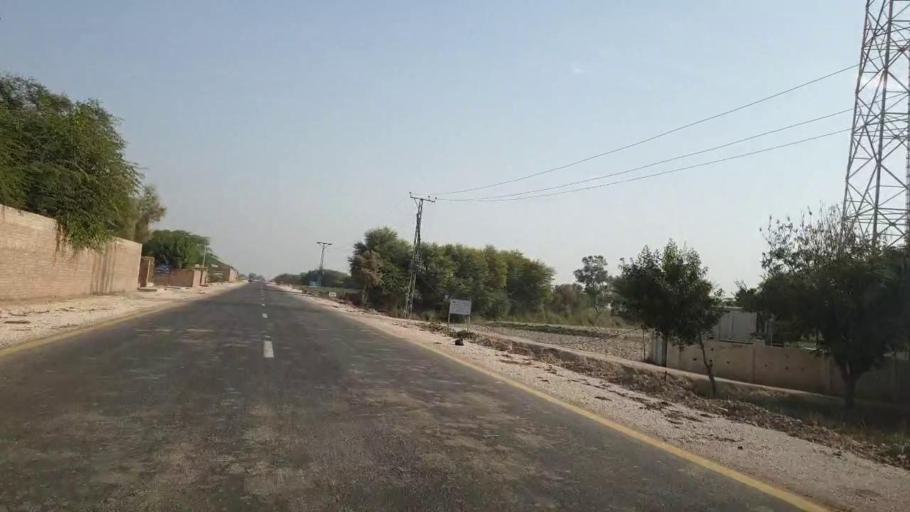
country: PK
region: Sindh
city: Sehwan
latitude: 26.4812
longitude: 67.7813
